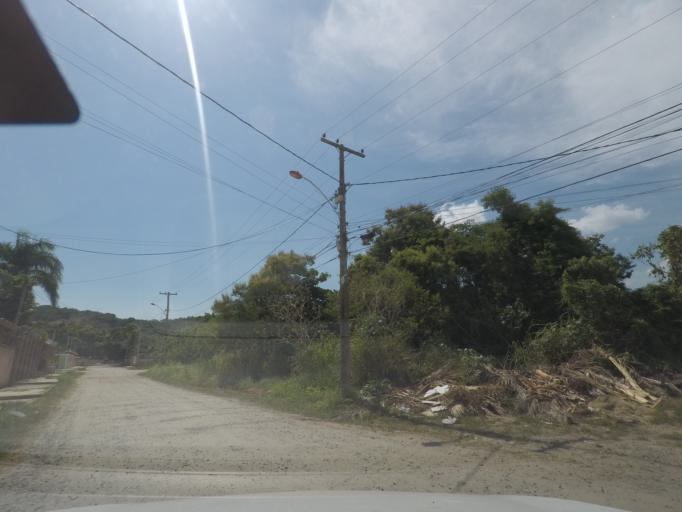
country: BR
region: Rio de Janeiro
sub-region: Marica
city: Marica
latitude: -22.9545
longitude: -42.9644
